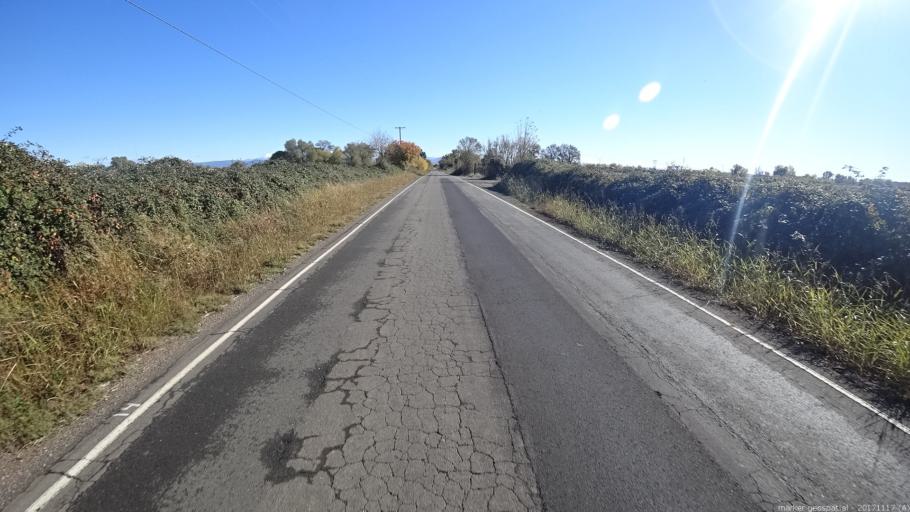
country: US
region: California
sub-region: Shasta County
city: Anderson
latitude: 40.4305
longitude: -122.2527
